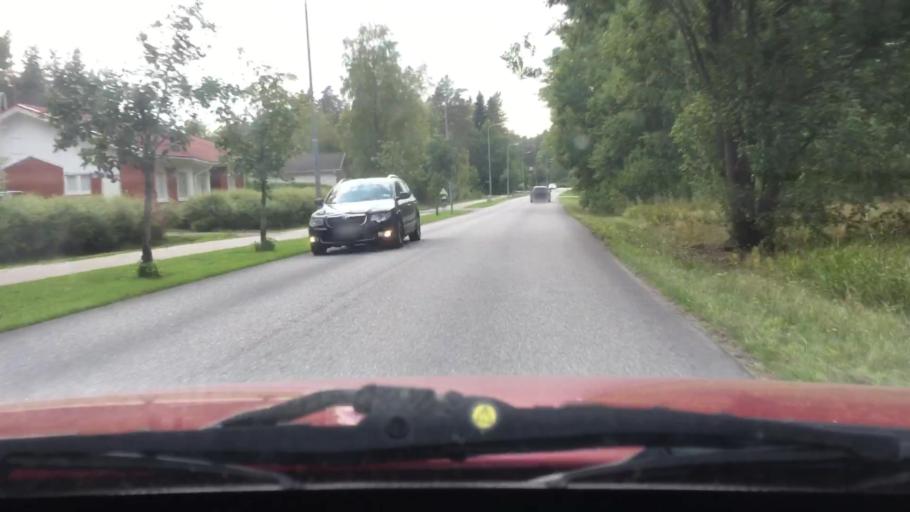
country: FI
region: Varsinais-Suomi
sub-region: Turku
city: Masku
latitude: 60.5579
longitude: 22.1408
